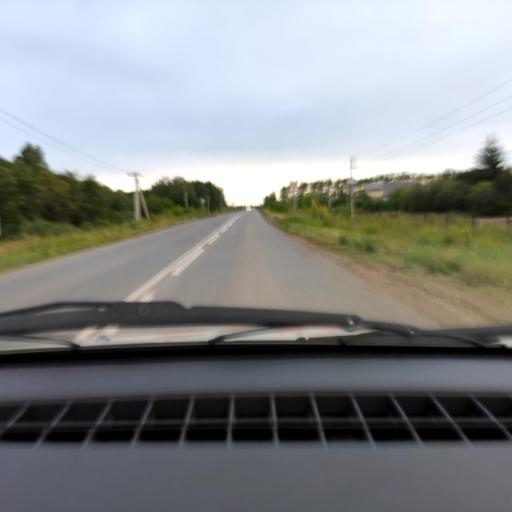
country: RU
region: Bashkortostan
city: Avdon
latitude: 54.5763
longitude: 55.7532
